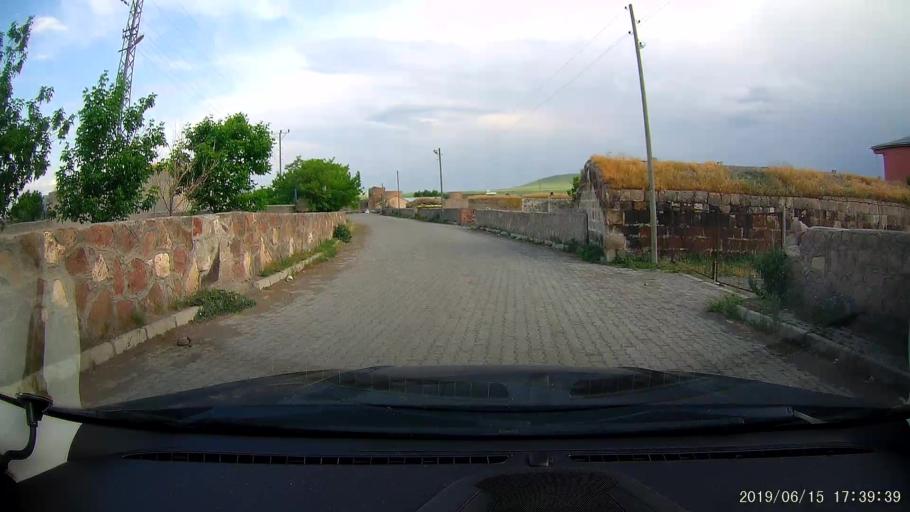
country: TR
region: Kars
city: Basgedikler
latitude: 40.5150
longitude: 43.5708
